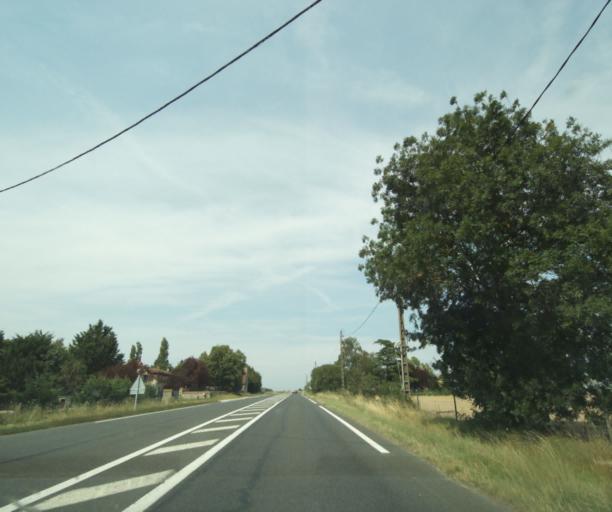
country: FR
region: Centre
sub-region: Departement d'Indre-et-Loire
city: Sainte-Maure-de-Touraine
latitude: 47.1728
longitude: 0.6550
